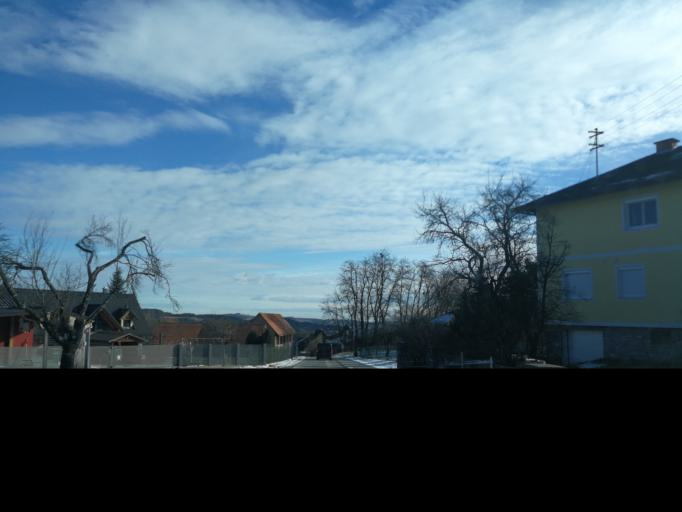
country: AT
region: Styria
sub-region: Politischer Bezirk Weiz
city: Ungerdorf
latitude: 47.1019
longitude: 15.6279
